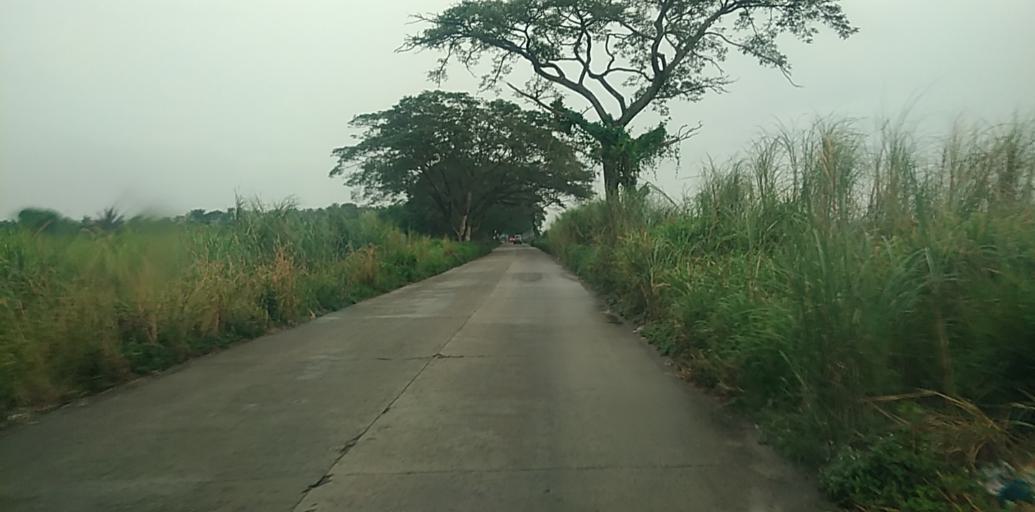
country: PH
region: Central Luzon
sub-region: Province of Pampanga
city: San Antonio
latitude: 15.1575
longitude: 120.6952
